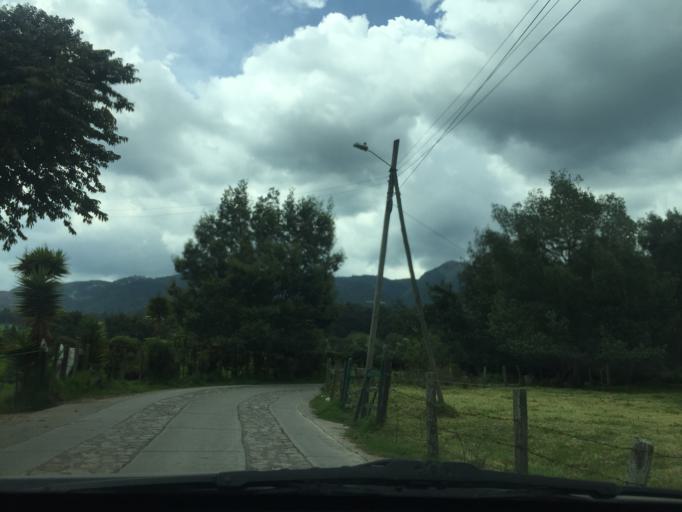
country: CO
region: Cundinamarca
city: Cogua
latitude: 5.0513
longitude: -73.9916
